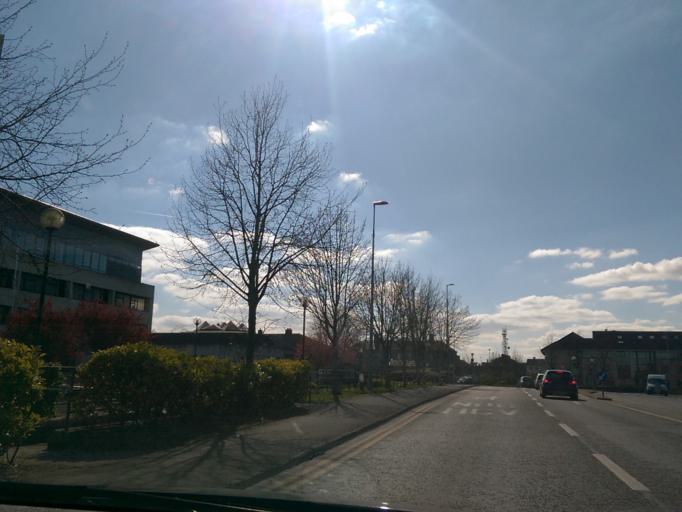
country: IE
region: Leinster
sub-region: Laois
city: Portlaoise
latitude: 53.0326
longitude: -7.3007
